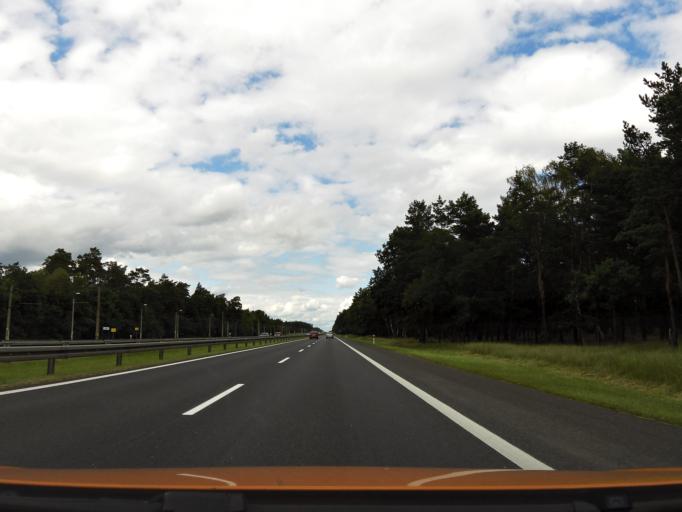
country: PL
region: West Pomeranian Voivodeship
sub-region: Powiat goleniowski
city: Goleniow
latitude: 53.4936
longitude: 14.7964
